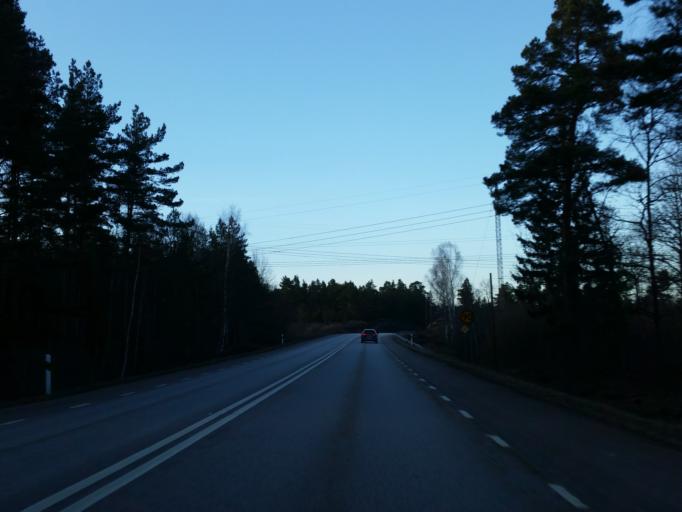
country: SE
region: Kalmar
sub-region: Oskarshamns Kommun
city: Oskarshamn
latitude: 57.4367
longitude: 16.4910
